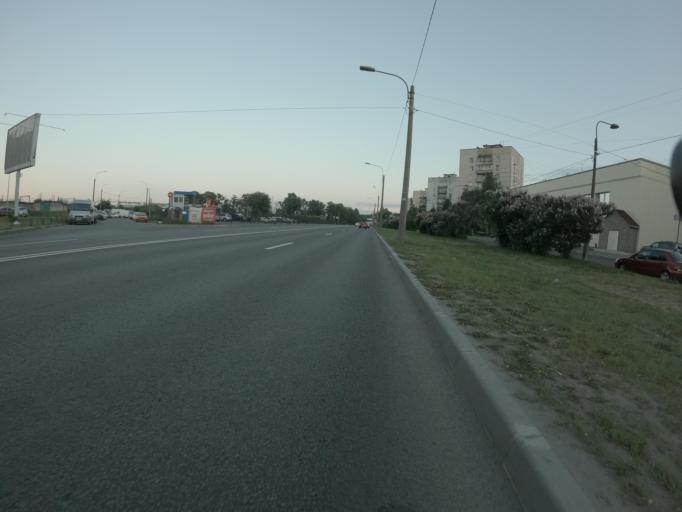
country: RU
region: St.-Petersburg
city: Dachnoye
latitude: 59.8490
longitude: 30.2804
